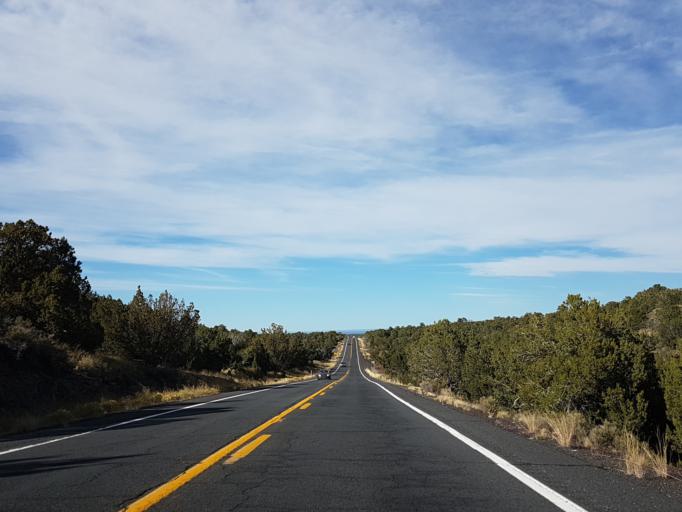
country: US
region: Arizona
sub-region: Coconino County
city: Williams
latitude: 35.4236
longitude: -112.1705
